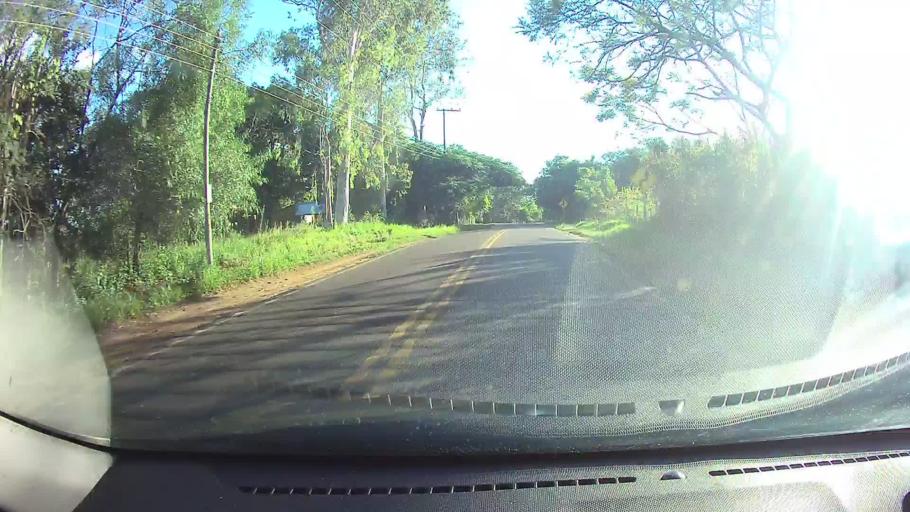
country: PY
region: Cordillera
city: Emboscada
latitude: -25.2003
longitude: -57.3224
